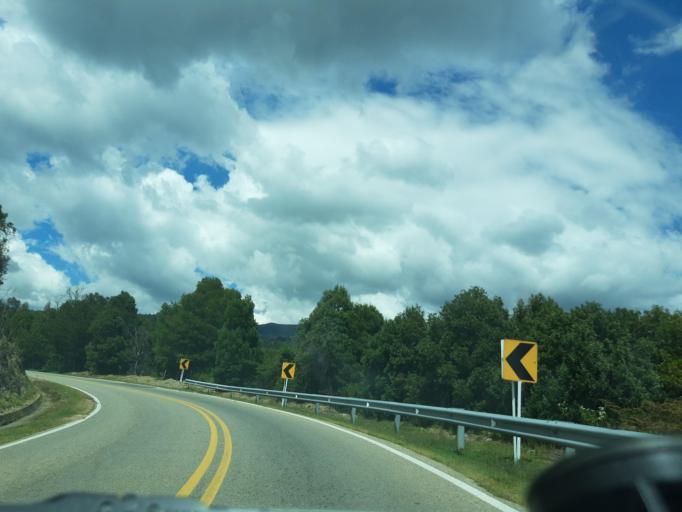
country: CO
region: Boyaca
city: Raquira
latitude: 5.5848
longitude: -73.6849
